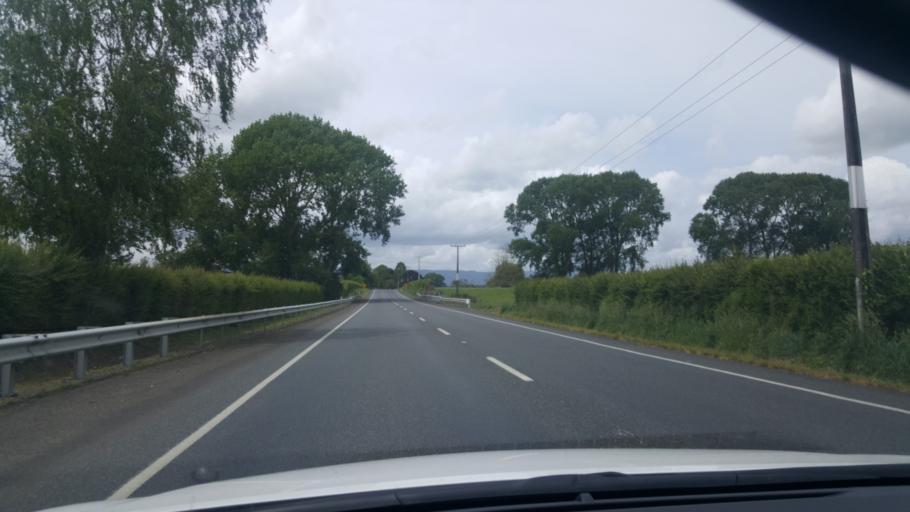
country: NZ
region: Waikato
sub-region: Matamata-Piako District
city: Matamata
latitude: -37.8802
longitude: 175.7482
